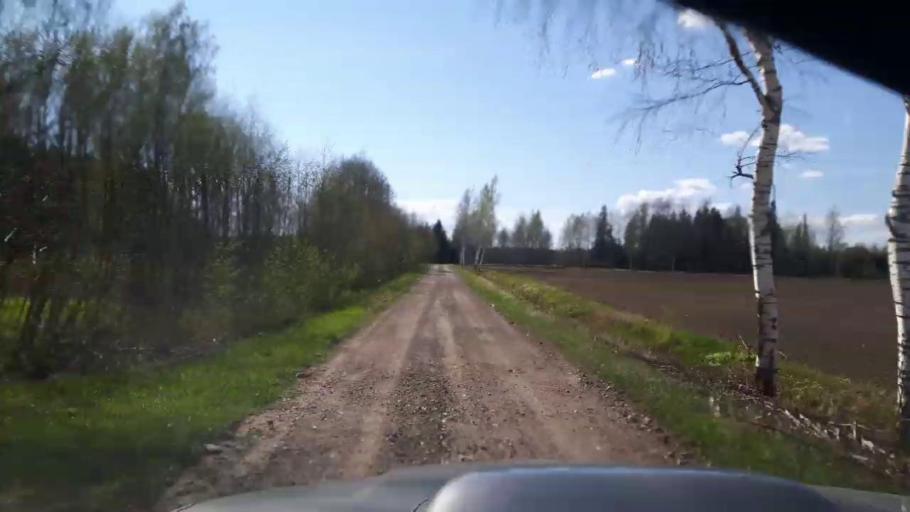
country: EE
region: Paernumaa
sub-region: Tootsi vald
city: Tootsi
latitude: 58.4496
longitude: 24.8458
